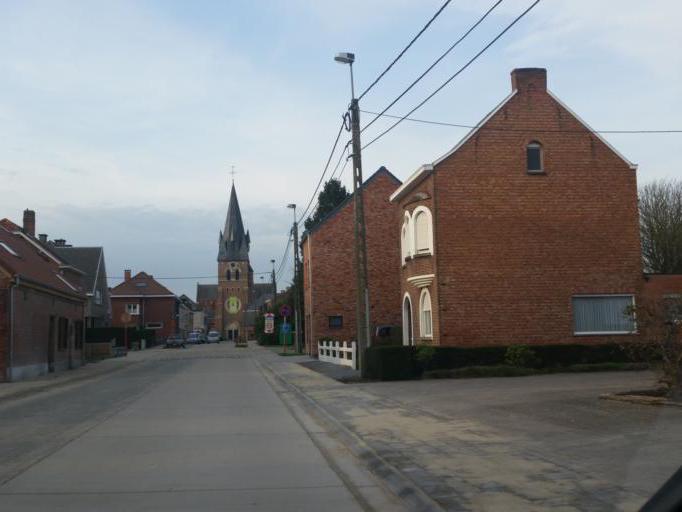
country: BE
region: Flanders
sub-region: Provincie Antwerpen
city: Mechelen
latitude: 51.0586
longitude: 4.4866
